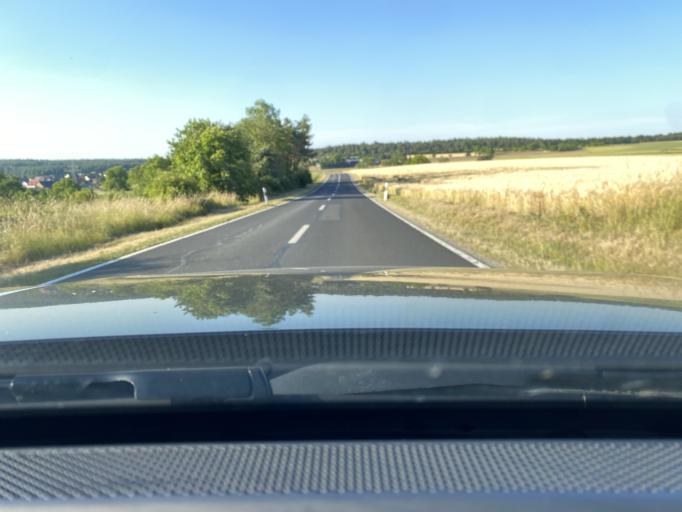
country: DE
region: Bavaria
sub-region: Regierungsbezirk Unterfranken
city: Roden
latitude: 49.9351
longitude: 9.6313
